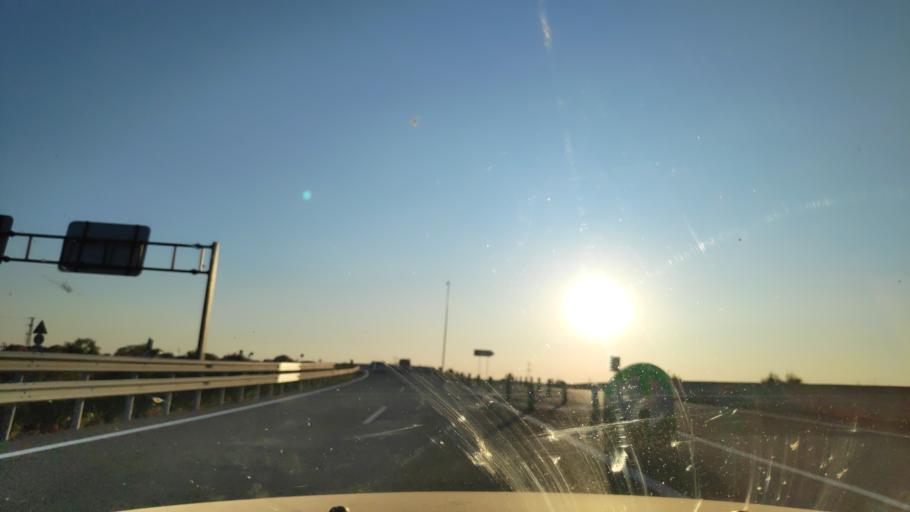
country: ES
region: Madrid
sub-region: Provincia de Madrid
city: Arganda
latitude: 40.2678
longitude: -3.3957
